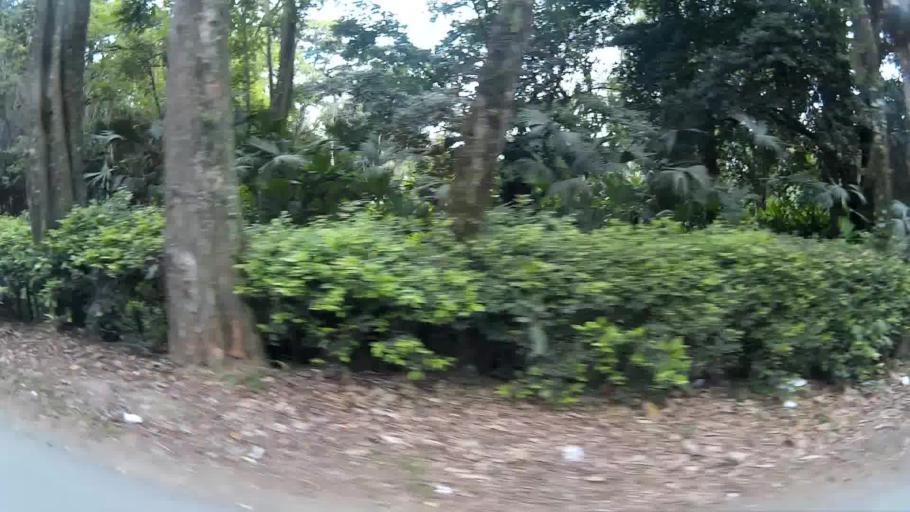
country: CO
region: Risaralda
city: La Virginia
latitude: 4.8926
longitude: -75.8787
